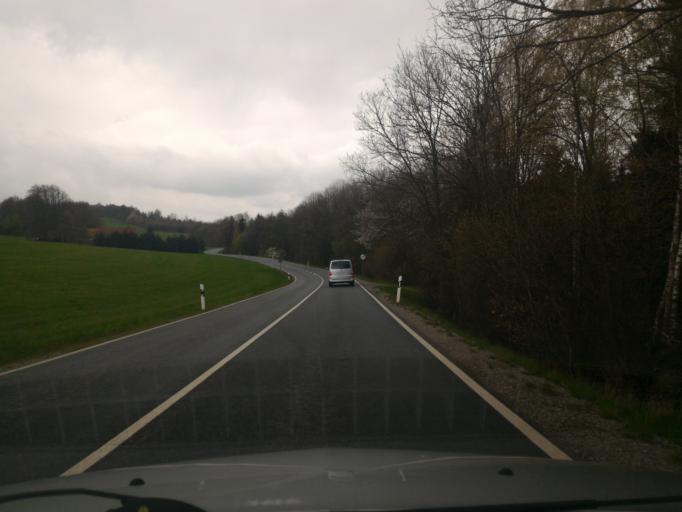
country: DE
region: Saxony
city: Leutersdorf
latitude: 50.9351
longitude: 14.6467
